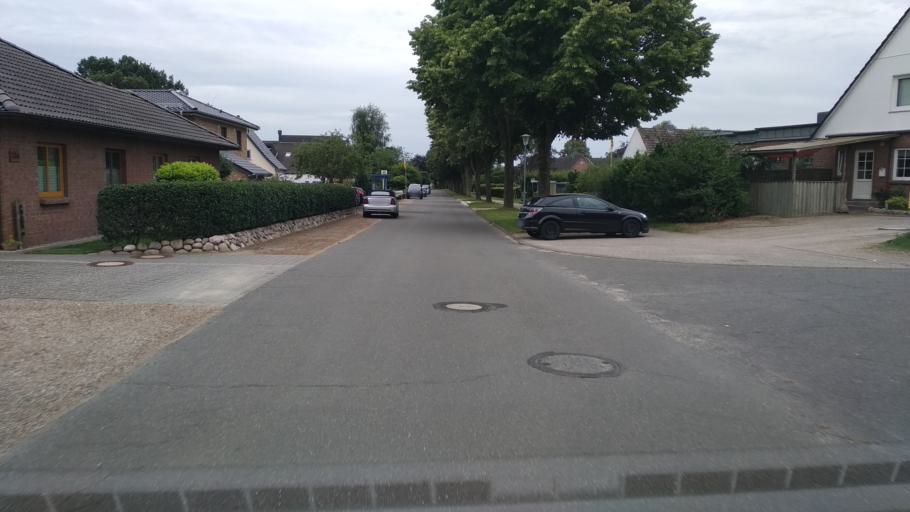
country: DE
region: Schleswig-Holstein
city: Schuby
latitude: 54.5245
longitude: 9.4828
